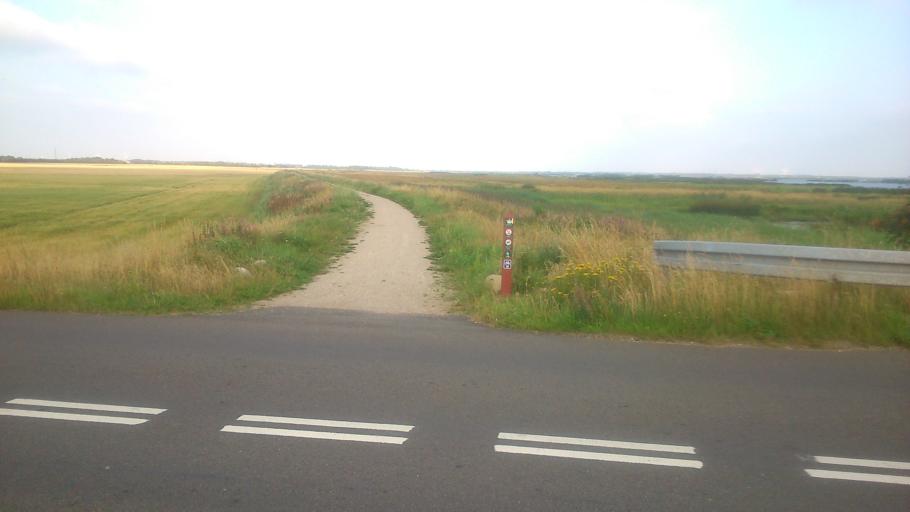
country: DK
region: Central Jutland
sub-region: Ringkobing-Skjern Kommune
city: Skjern
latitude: 55.9270
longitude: 8.4404
